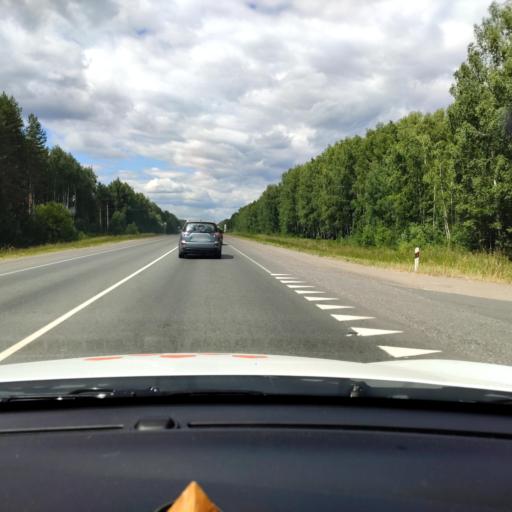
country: RU
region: Mariy-El
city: Pomary
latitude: 55.9374
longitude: 48.3717
